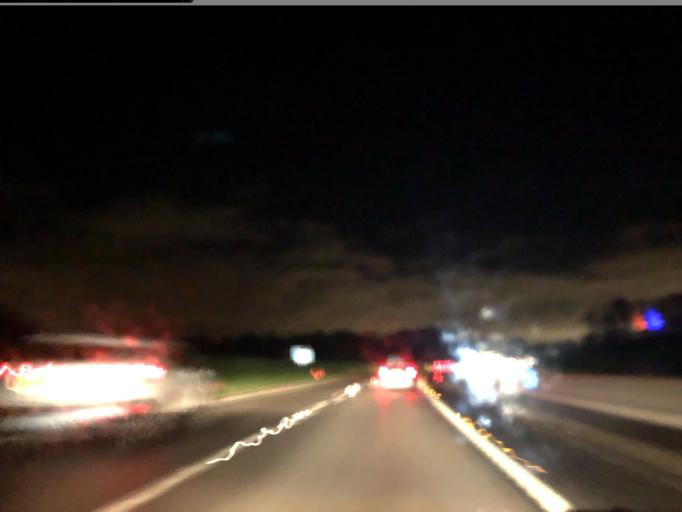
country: GB
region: England
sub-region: Cheshire East
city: Mere
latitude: 53.3284
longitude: -2.4226
